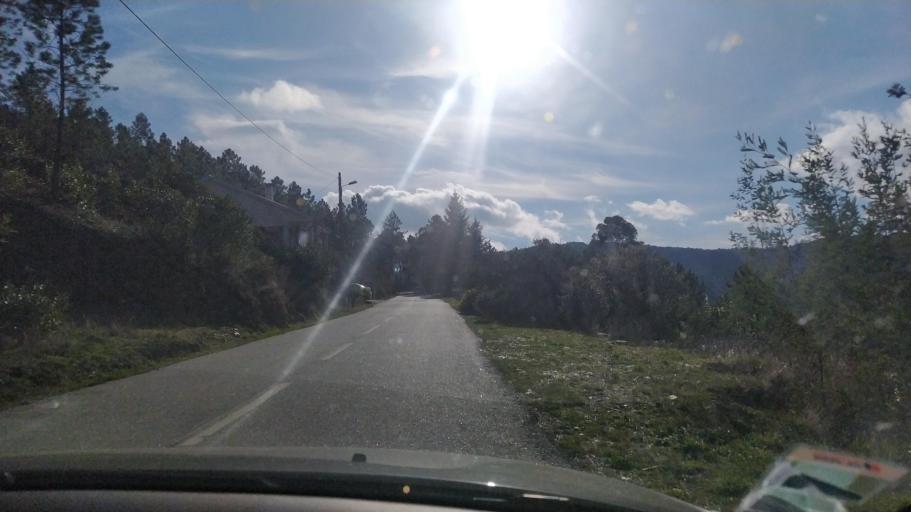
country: PT
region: Coimbra
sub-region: Oliveira do Hospital
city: Oliveira do Hospital
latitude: 40.2051
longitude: -7.7382
